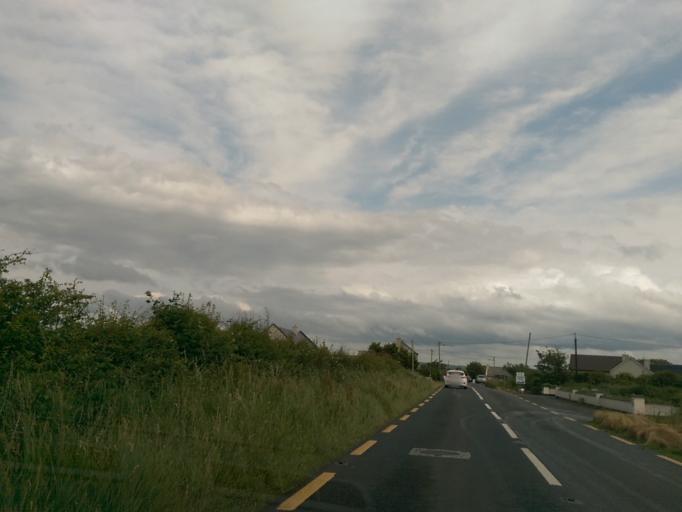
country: IE
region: Munster
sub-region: An Clar
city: Kilrush
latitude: 52.7353
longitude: -9.4993
